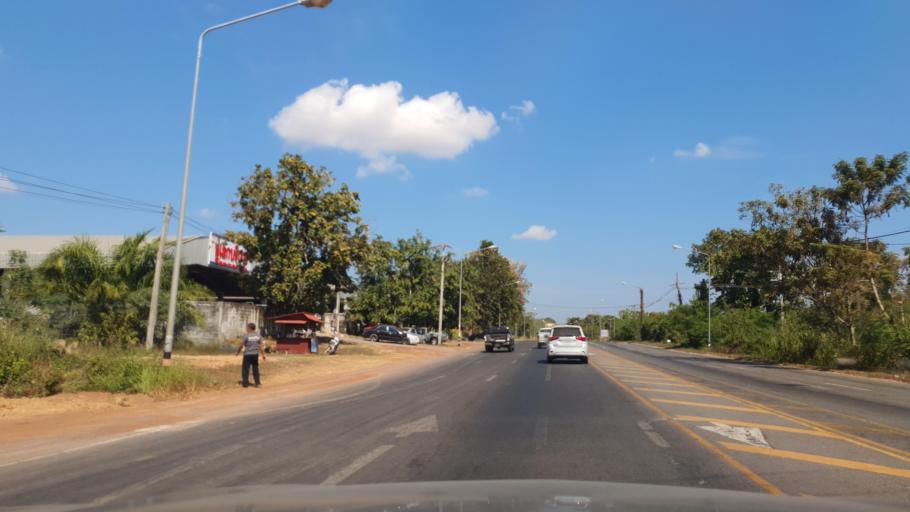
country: TH
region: Kalasin
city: Somdet
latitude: 16.7420
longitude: 103.7705
